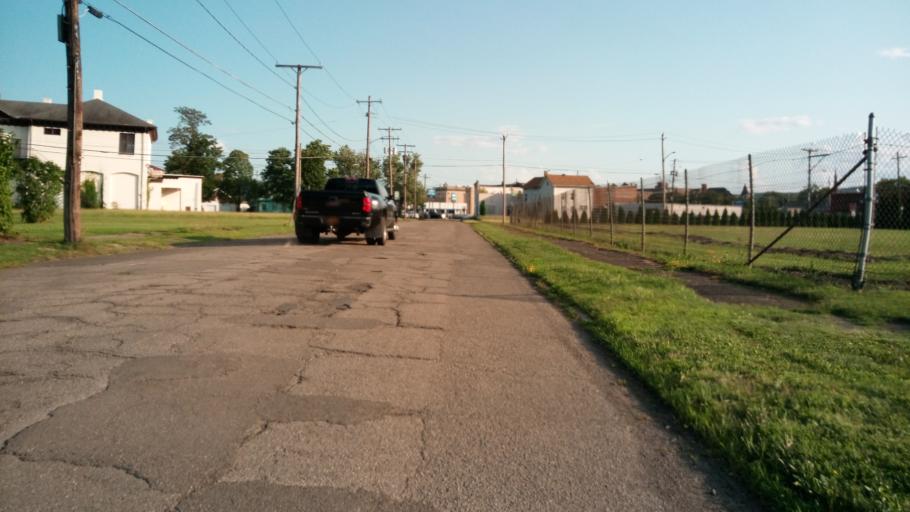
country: US
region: New York
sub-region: Chemung County
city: Elmira
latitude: 42.0944
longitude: -76.8047
